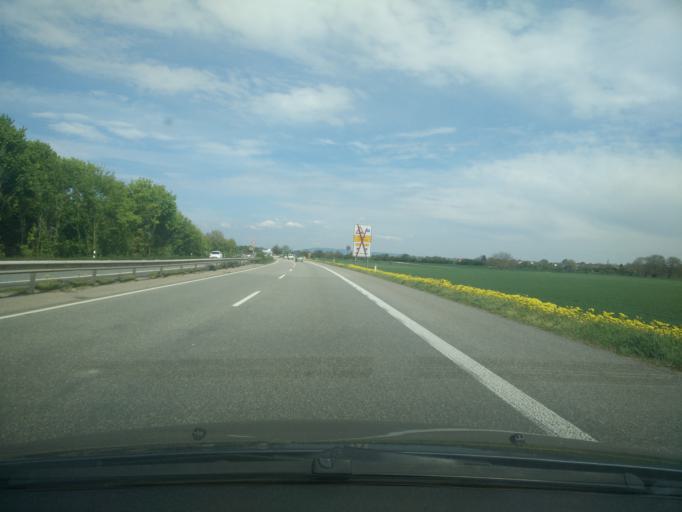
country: DE
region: Rheinland-Pfalz
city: Dudenhofen
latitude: 49.2939
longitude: 8.3881
